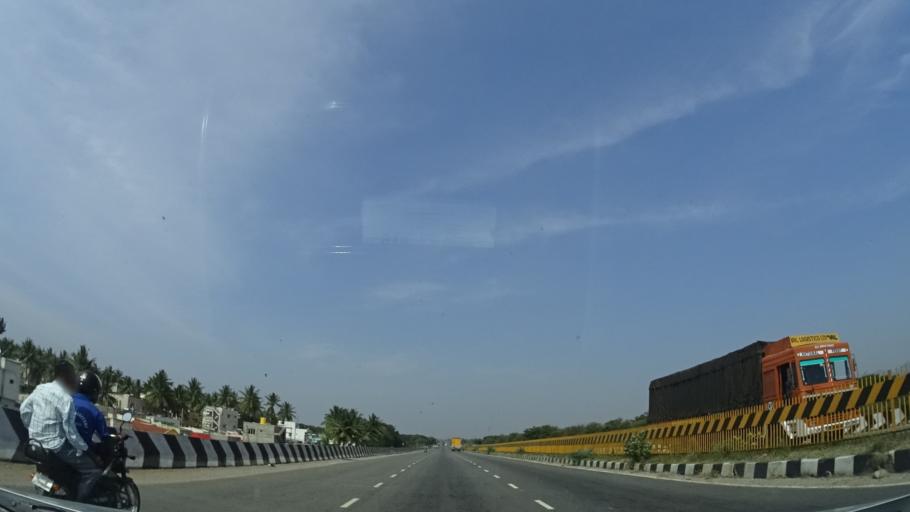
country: IN
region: Karnataka
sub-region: Tumkur
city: Tumkur
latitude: 13.3363
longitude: 77.1286
